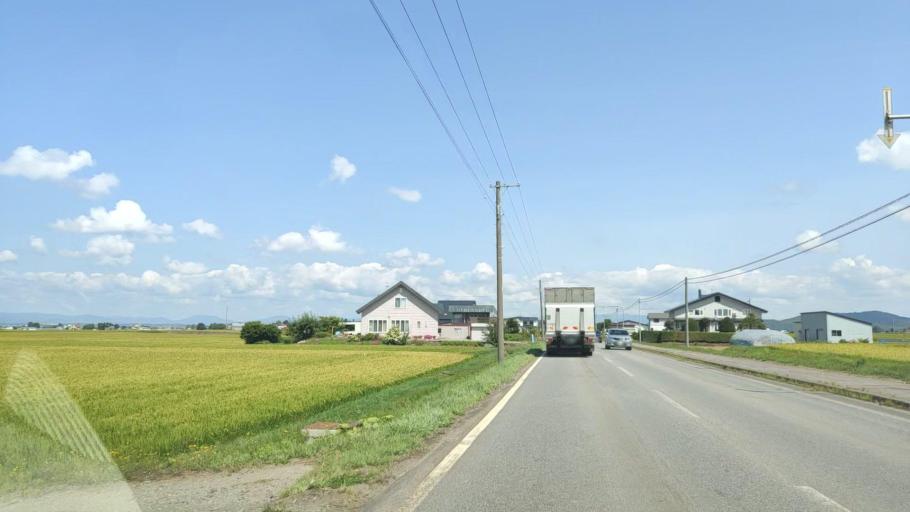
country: JP
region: Hokkaido
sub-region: Asahikawa-shi
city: Asahikawa
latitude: 43.7188
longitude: 142.4576
